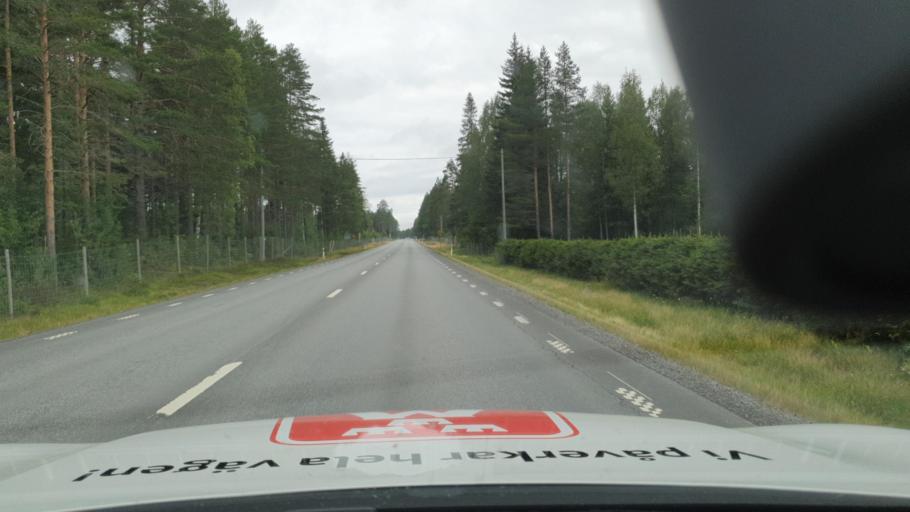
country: SE
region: Vaesterbotten
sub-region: Skelleftea Kommun
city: Burea
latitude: 64.5444
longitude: 21.2517
